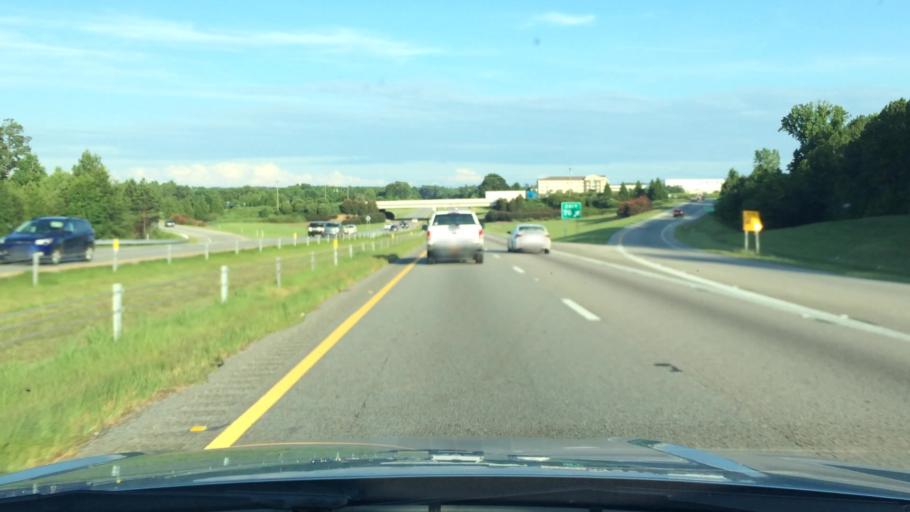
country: US
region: South Carolina
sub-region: Newberry County
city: Newberry
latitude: 34.2952
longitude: -81.5490
